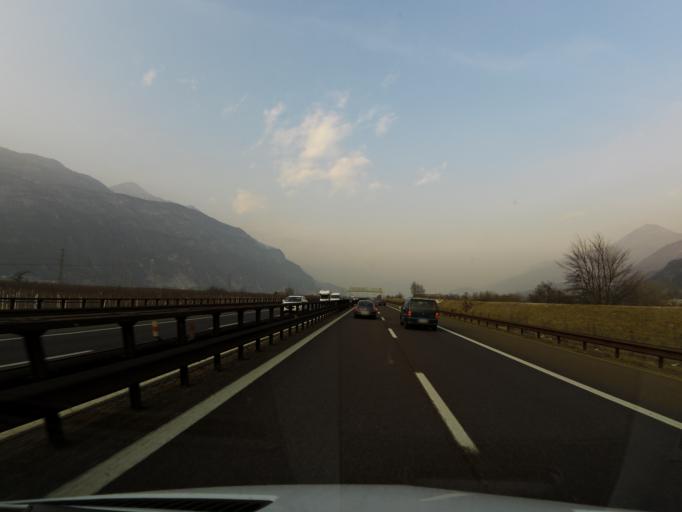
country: IT
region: Trentino-Alto Adige
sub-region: Provincia di Trento
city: Aldeno
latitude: 45.9743
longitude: 11.1081
